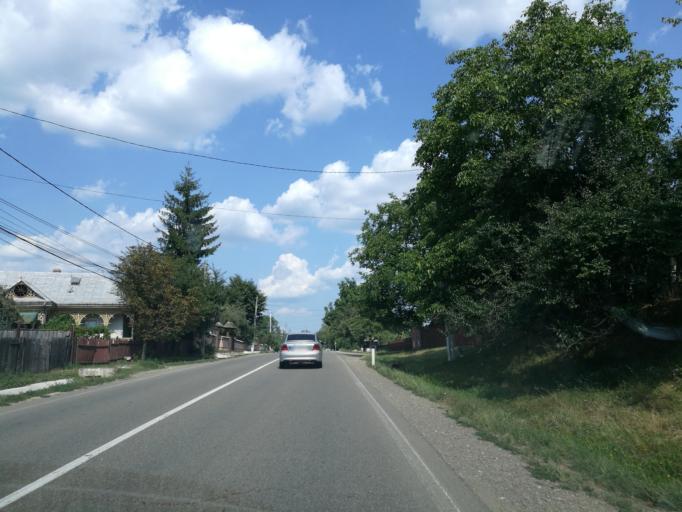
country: RO
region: Neamt
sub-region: Comuna Baltatesti
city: Valea Seaca
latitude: 47.1322
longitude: 26.3152
